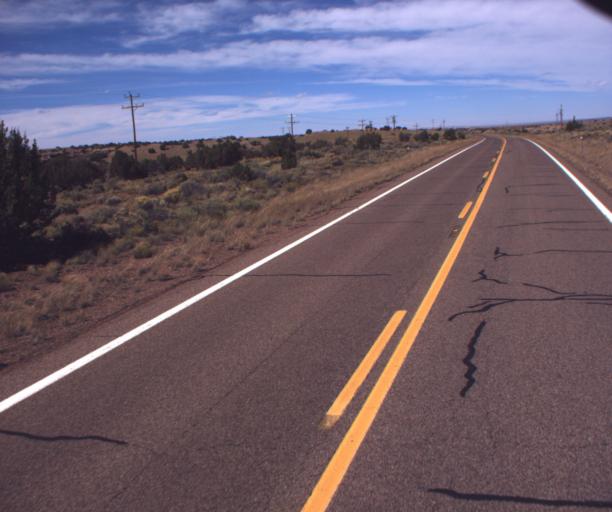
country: US
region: Arizona
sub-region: Apache County
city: Saint Johns
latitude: 34.5341
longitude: -109.6203
